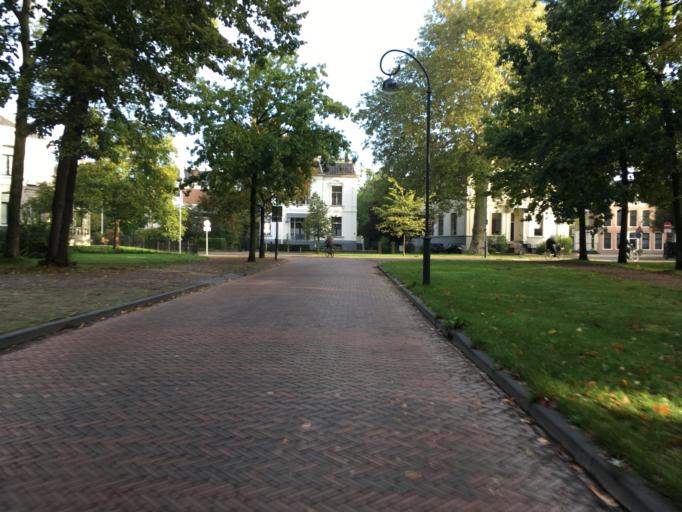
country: NL
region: North Holland
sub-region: Gemeente Haarlem
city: Haarlem
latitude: 52.3872
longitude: 4.6330
